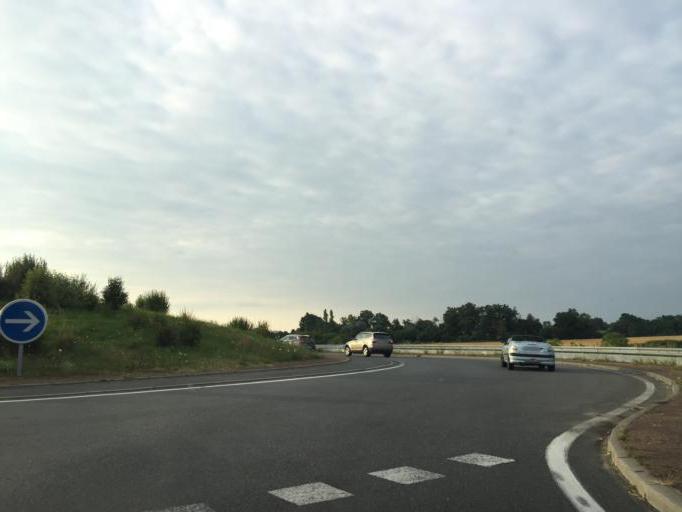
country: FR
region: Auvergne
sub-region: Departement de l'Allier
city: Varennes-sur-Allier
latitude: 46.3558
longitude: 3.3751
